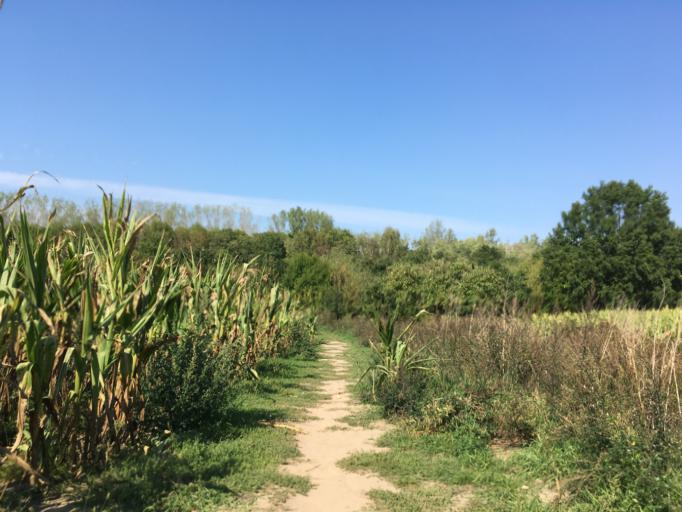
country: DE
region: Berlin
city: Buchholz
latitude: 52.6307
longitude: 13.4195
